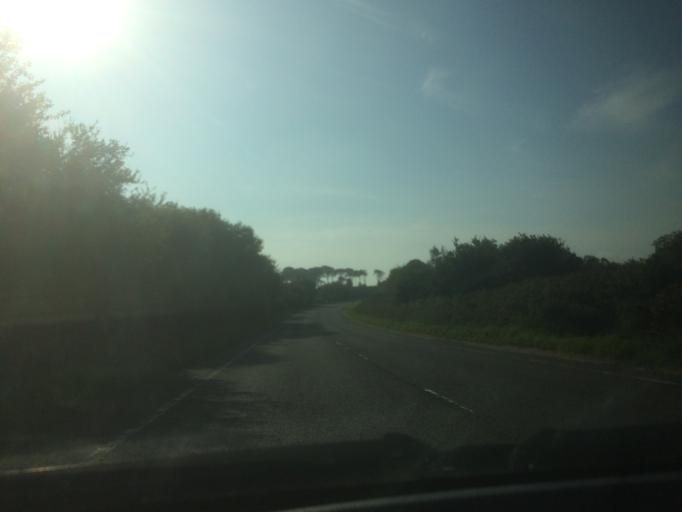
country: GB
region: England
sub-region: Cornwall
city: Pillaton
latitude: 50.4614
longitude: -4.2634
